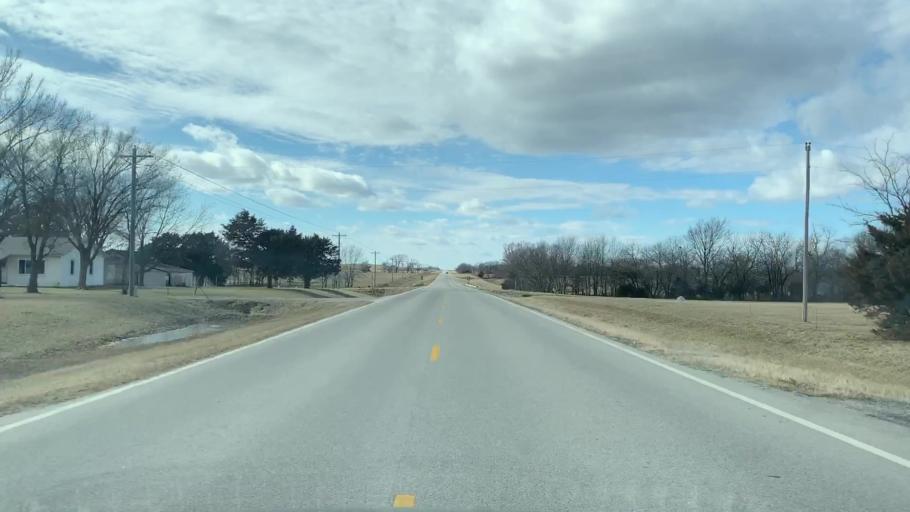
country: US
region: Kansas
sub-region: Neosho County
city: Erie
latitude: 37.5294
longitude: -95.3422
